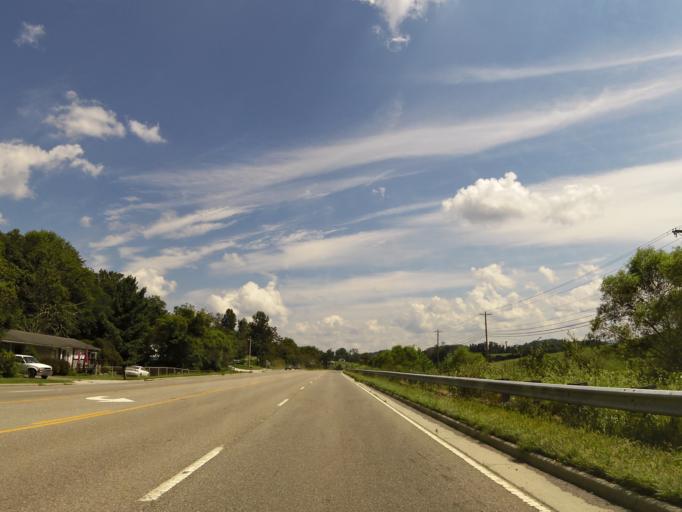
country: US
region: Virginia
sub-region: Washington County
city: Abingdon
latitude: 36.7054
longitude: -81.9193
